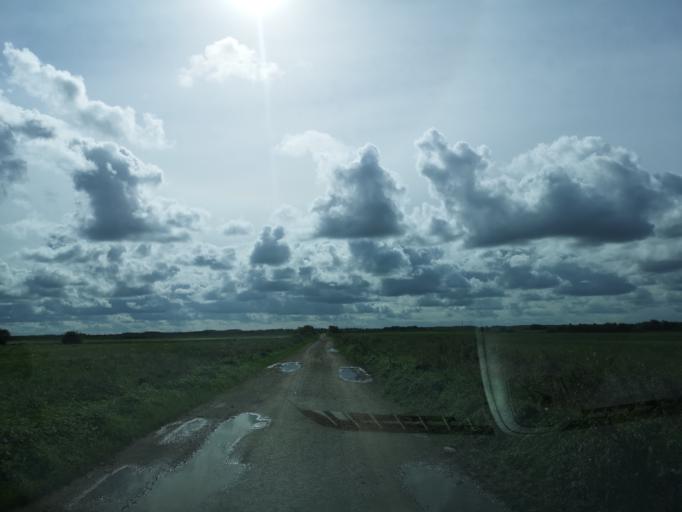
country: DK
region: Central Jutland
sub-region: Ringkobing-Skjern Kommune
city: Tarm
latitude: 55.9351
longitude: 8.5371
